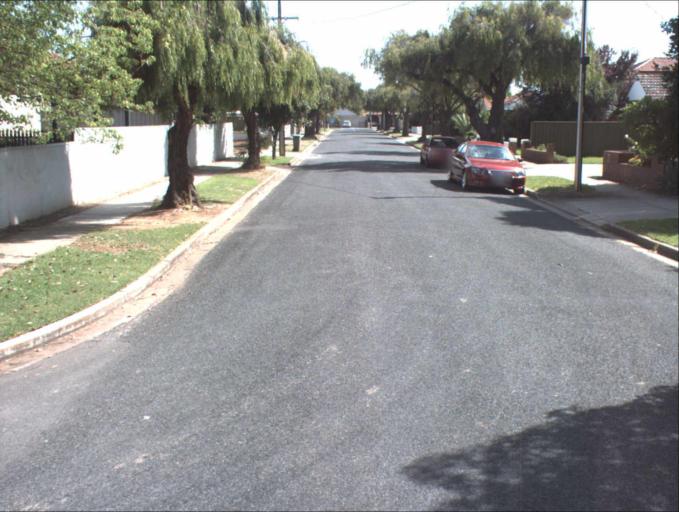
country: AU
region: South Australia
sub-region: Port Adelaide Enfield
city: Klemzig
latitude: -34.8804
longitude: 138.6217
